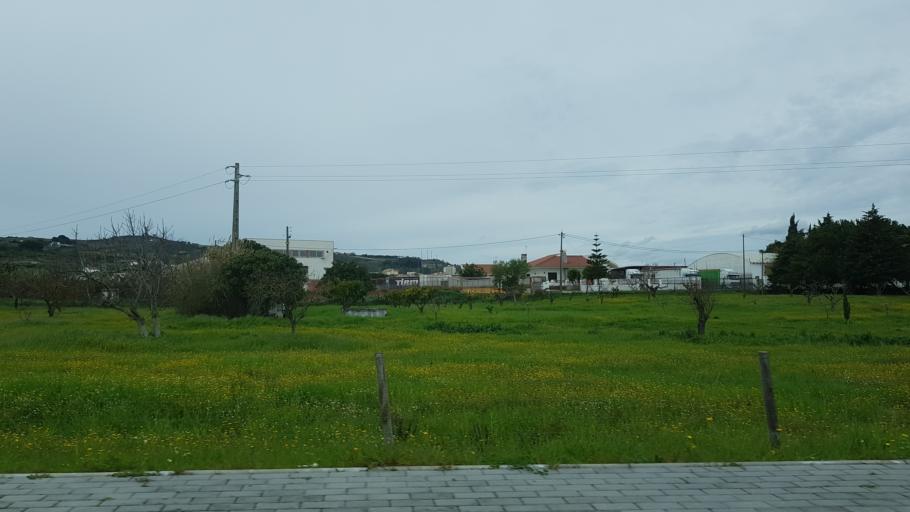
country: PT
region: Lisbon
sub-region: Alenquer
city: Carregado
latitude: 39.0380
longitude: -8.9903
